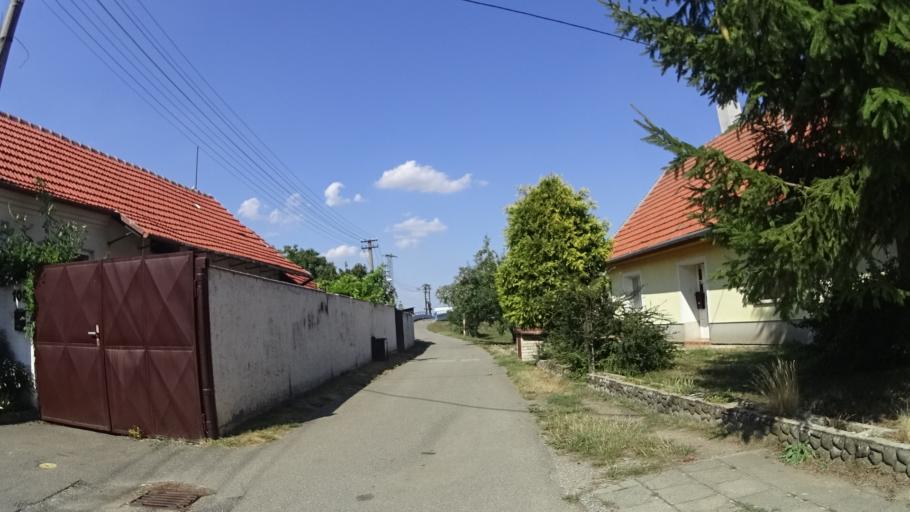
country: CZ
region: Zlin
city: Uhersky Ostroh
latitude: 48.9933
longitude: 17.4015
